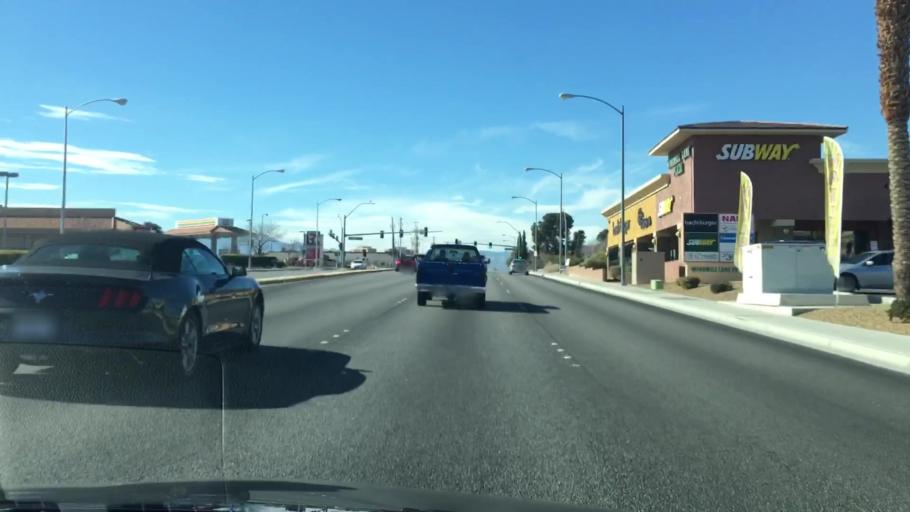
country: US
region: Nevada
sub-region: Clark County
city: Paradise
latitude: 36.0424
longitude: -115.1526
